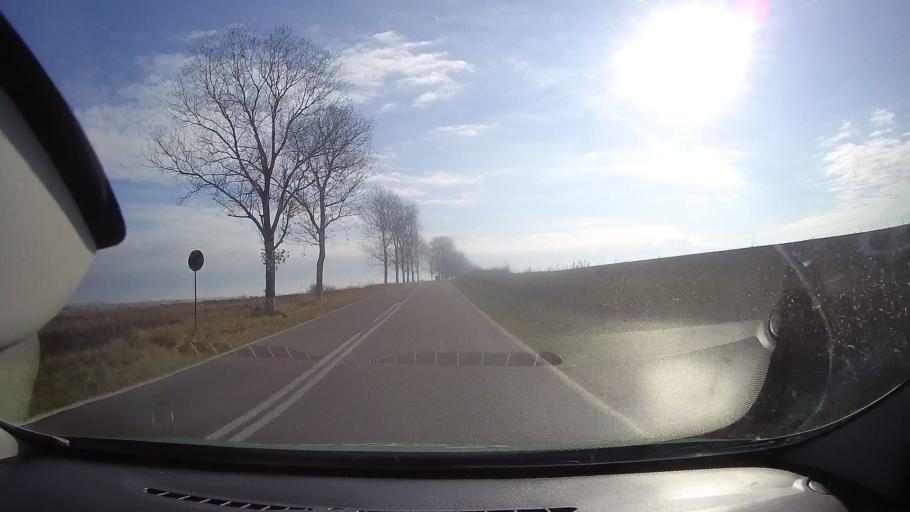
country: RO
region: Tulcea
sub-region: Comuna Mahmudia
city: Mahmudia
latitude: 45.0671
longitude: 29.1047
